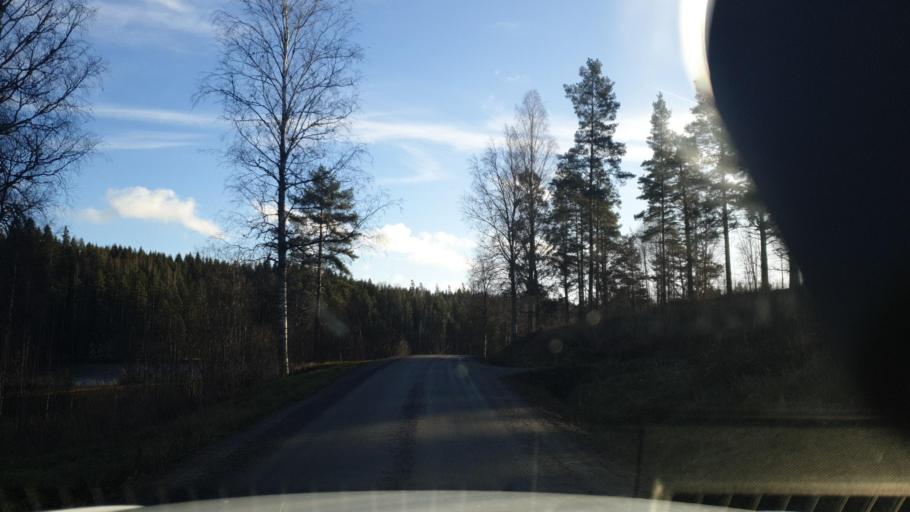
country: NO
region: Hedmark
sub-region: Eidskog
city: Skotterud
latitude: 59.8711
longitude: 11.9813
